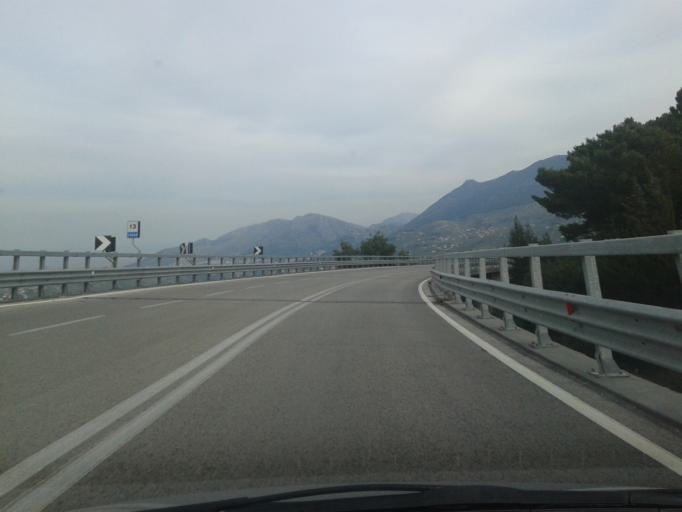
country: IT
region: Sicily
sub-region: Palermo
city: Giacalone
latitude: 38.0381
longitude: 13.2376
